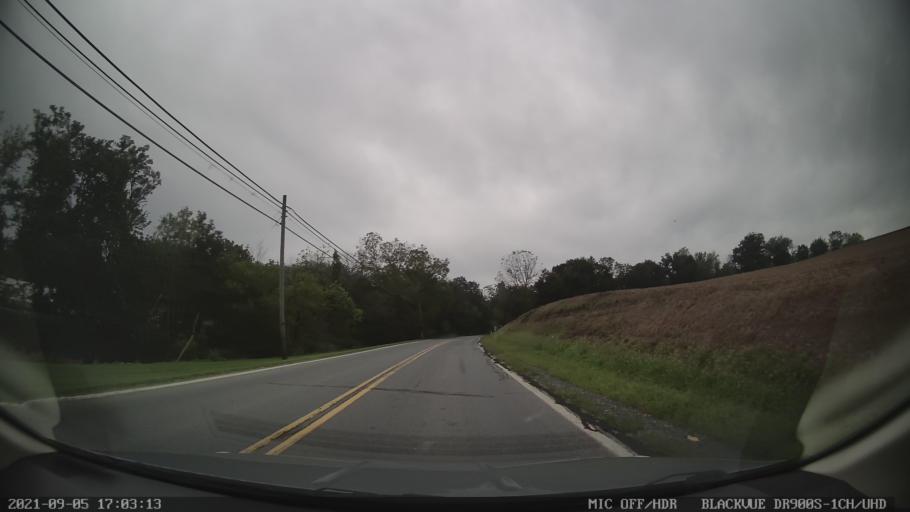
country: US
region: Pennsylvania
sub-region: Lehigh County
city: Breinigsville
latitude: 40.5767
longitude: -75.6651
